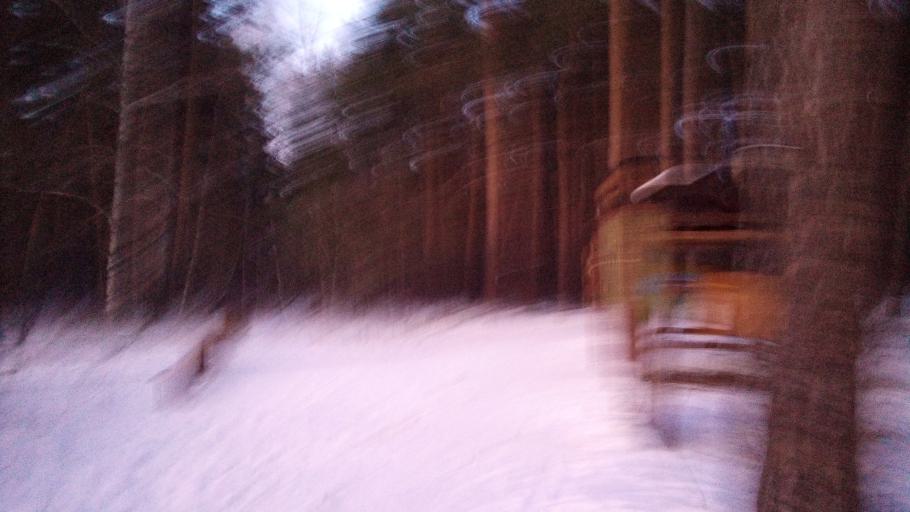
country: RU
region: Chelyabinsk
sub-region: Gorod Chelyabinsk
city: Chelyabinsk
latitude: 55.1653
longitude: 61.3316
